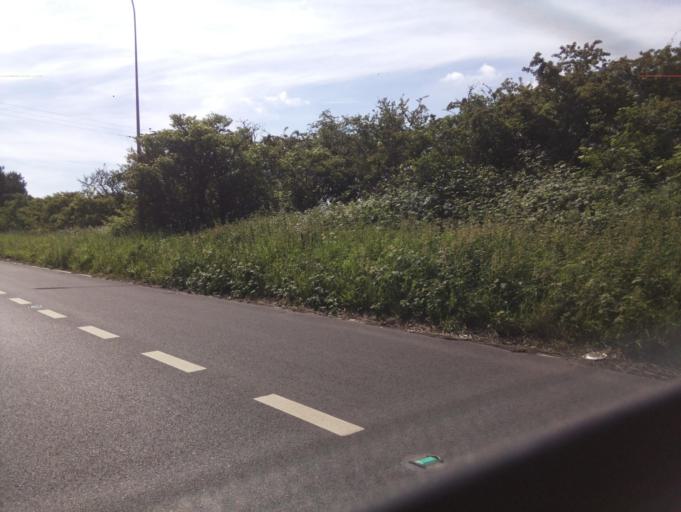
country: GB
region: England
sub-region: North Lincolnshire
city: Broughton
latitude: 53.5561
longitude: -0.5872
